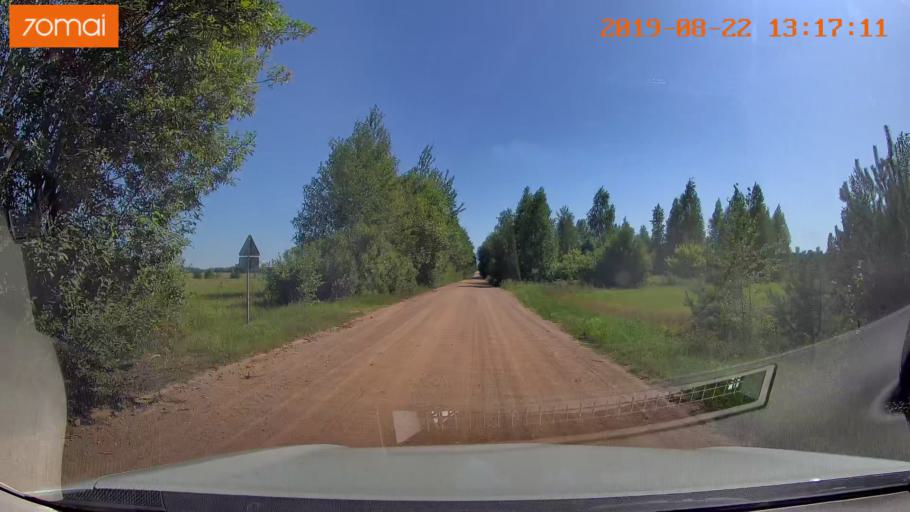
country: BY
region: Minsk
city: Prawdzinski
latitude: 53.2500
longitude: 27.9185
